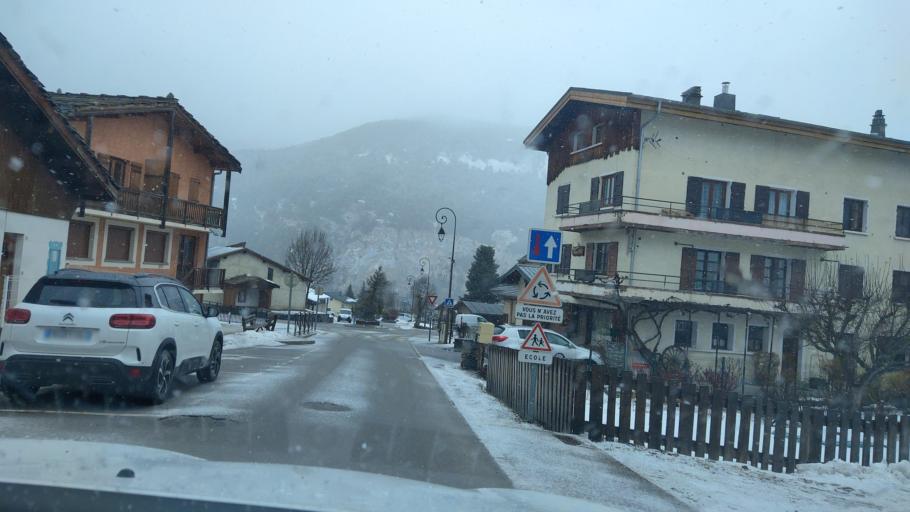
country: FR
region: Rhone-Alpes
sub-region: Departement de la Savoie
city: Modane
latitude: 45.2246
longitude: 6.7756
